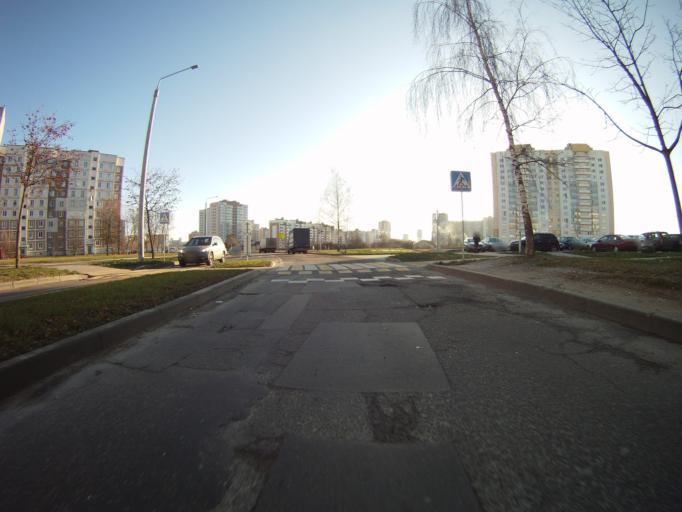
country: BY
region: Minsk
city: Novoye Medvezhino
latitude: 53.8803
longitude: 27.4404
